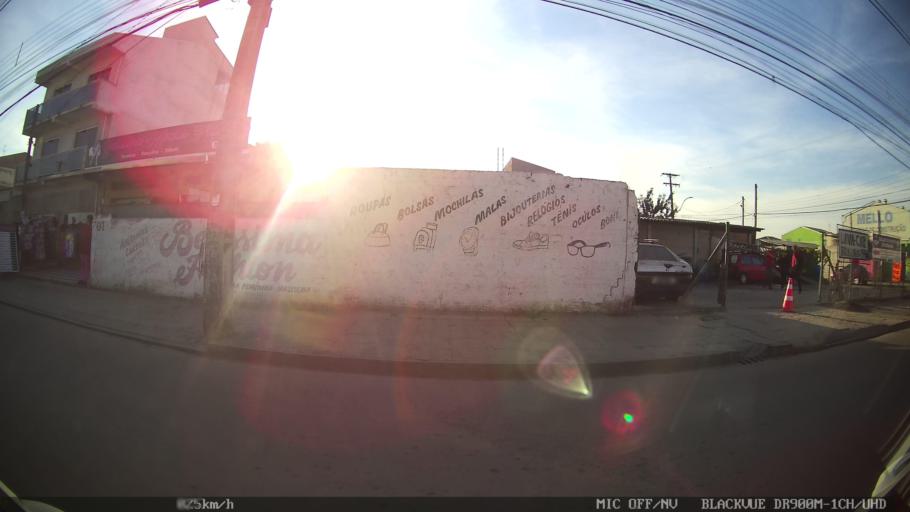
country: BR
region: Parana
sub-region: Pinhais
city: Pinhais
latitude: -25.4561
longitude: -49.1547
